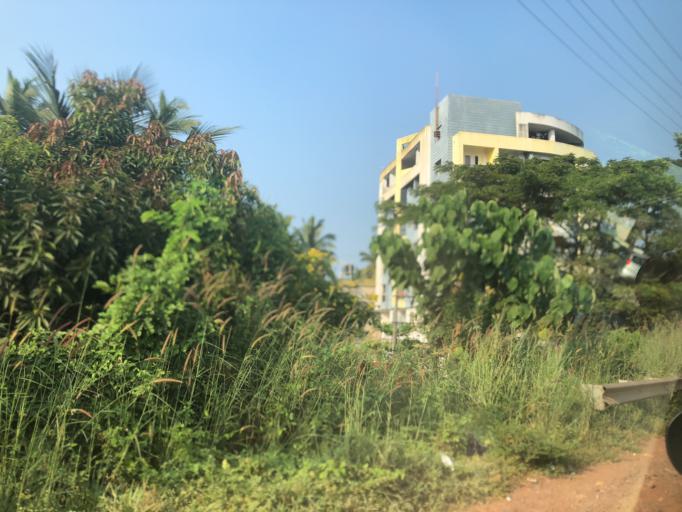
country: IN
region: Karnataka
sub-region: Dakshina Kannada
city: Ullal
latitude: 12.8201
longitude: 74.8698
